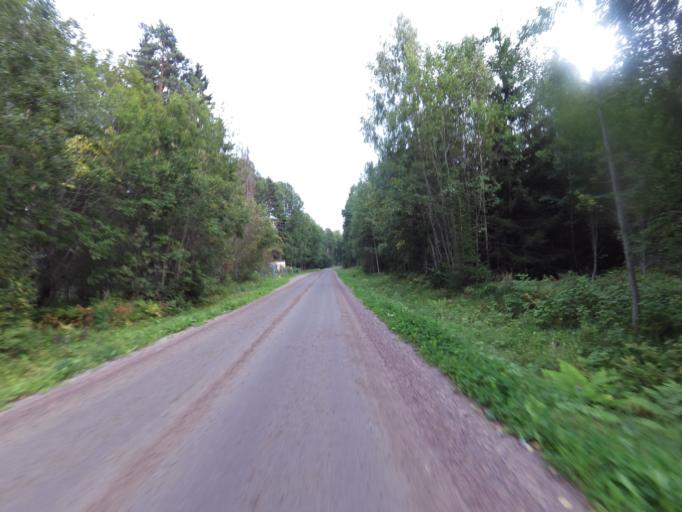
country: SE
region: Gaevleborg
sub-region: Gavle Kommun
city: Gavle
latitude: 60.7079
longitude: 17.1448
